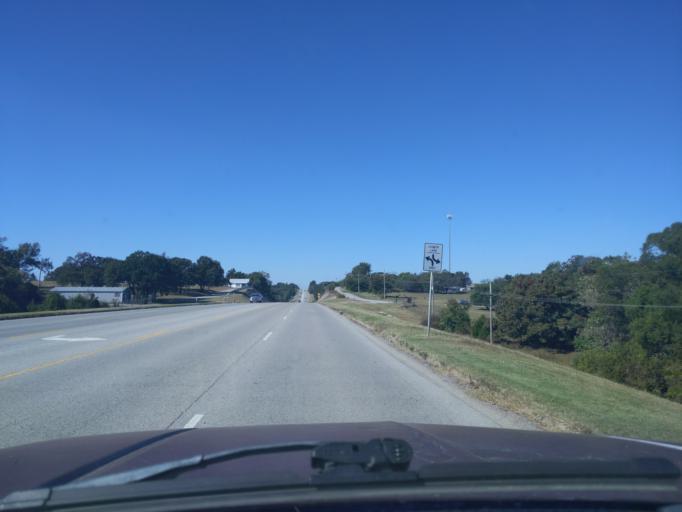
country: US
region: Oklahoma
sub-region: Creek County
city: Sapulpa
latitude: 35.9885
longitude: -96.0742
